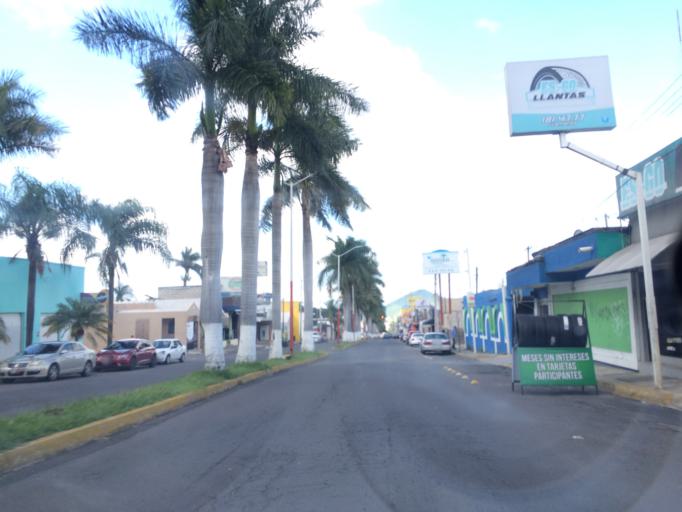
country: MX
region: Nayarit
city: Tepic
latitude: 21.5029
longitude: -104.9098
